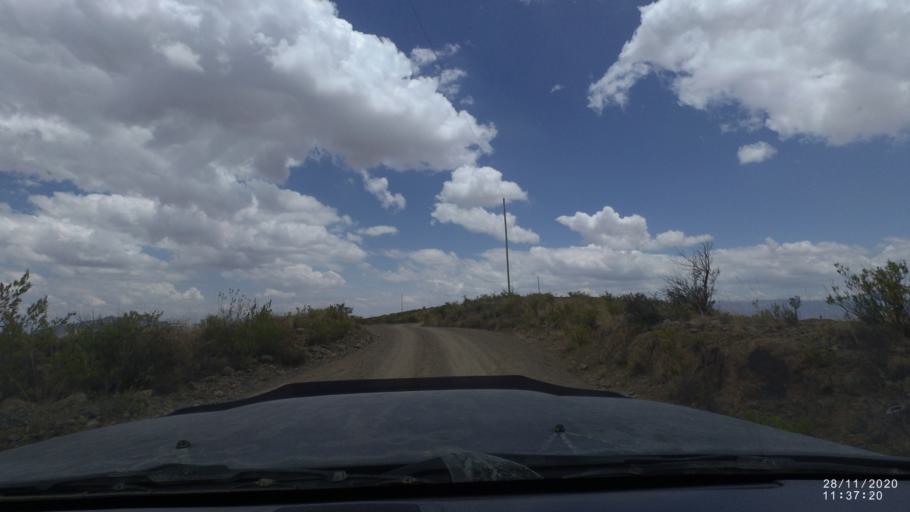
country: BO
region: Cochabamba
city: Tarata
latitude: -17.6791
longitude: -66.0433
